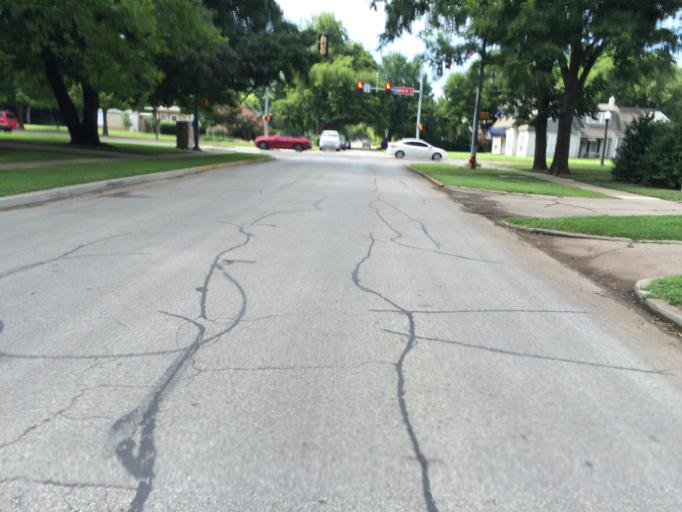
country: US
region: Oklahoma
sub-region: Cleveland County
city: Norman
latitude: 35.2116
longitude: -97.4501
